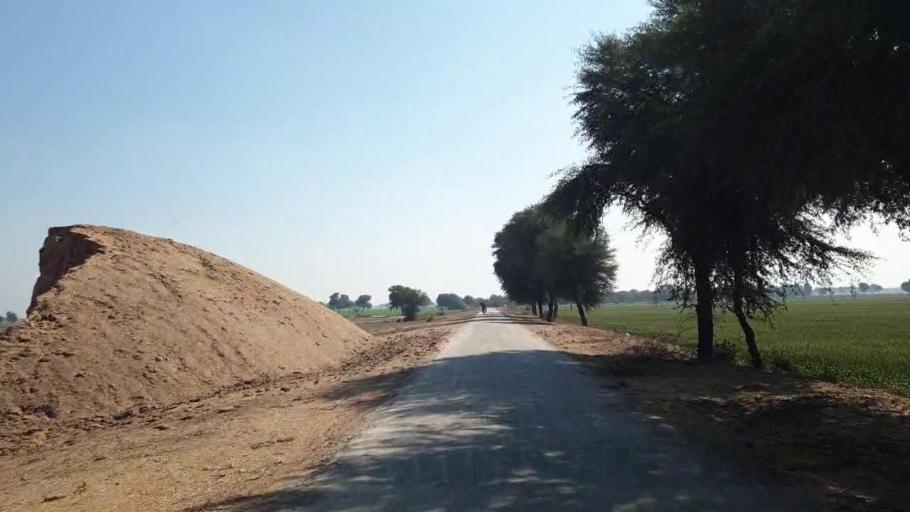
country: PK
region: Sindh
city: Shahpur Chakar
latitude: 26.1208
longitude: 68.6262
